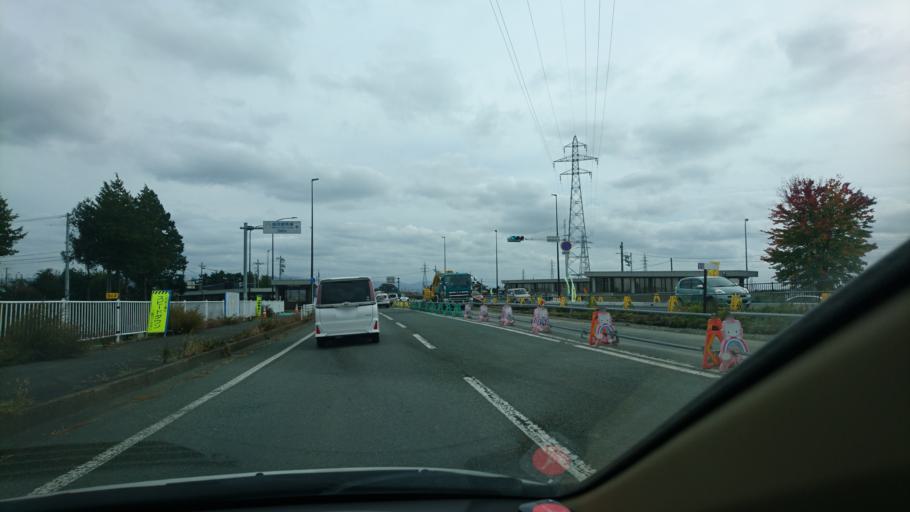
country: JP
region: Iwate
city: Morioka-shi
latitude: 39.6936
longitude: 141.1055
